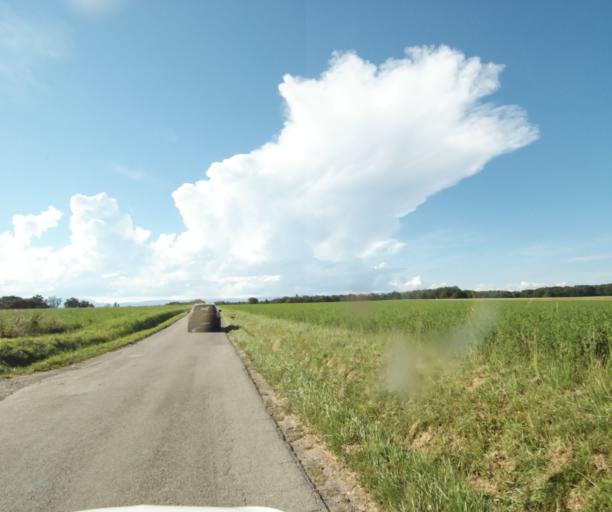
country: FR
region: Rhone-Alpes
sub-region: Departement de la Haute-Savoie
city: Douvaine
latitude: 46.3276
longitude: 6.3128
